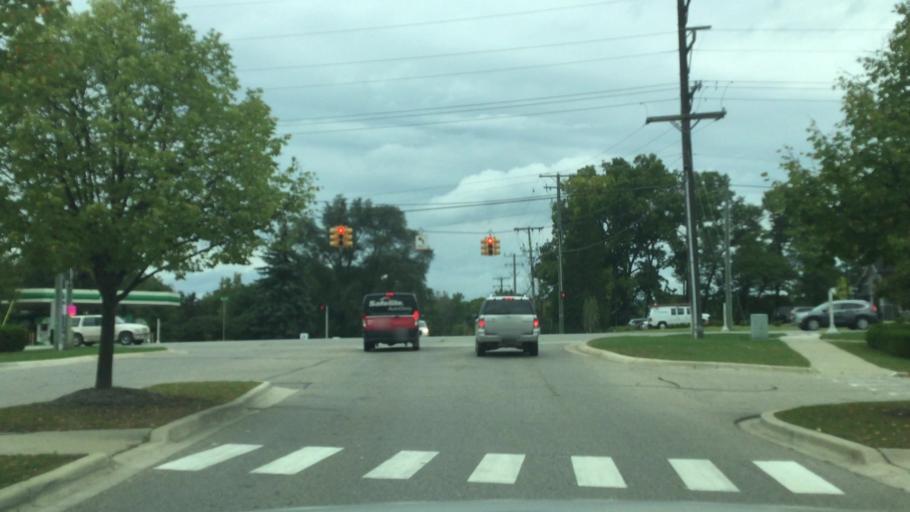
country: US
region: Michigan
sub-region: Livingston County
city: Brighton
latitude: 42.4629
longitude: -83.8334
